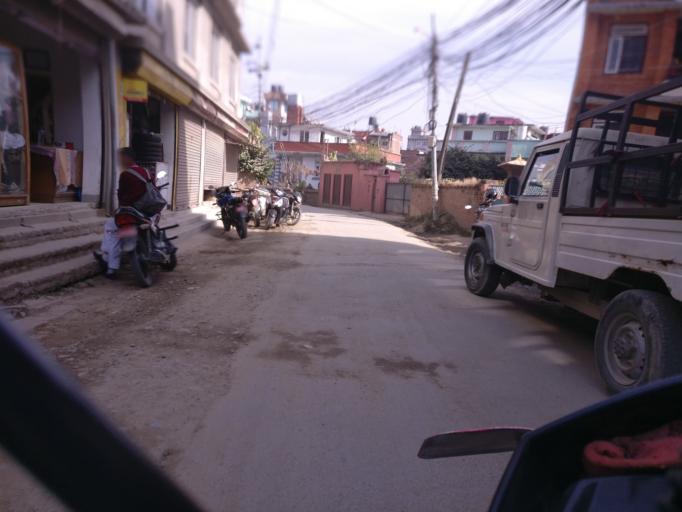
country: NP
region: Central Region
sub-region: Bagmati Zone
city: Patan
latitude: 27.6723
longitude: 85.3179
